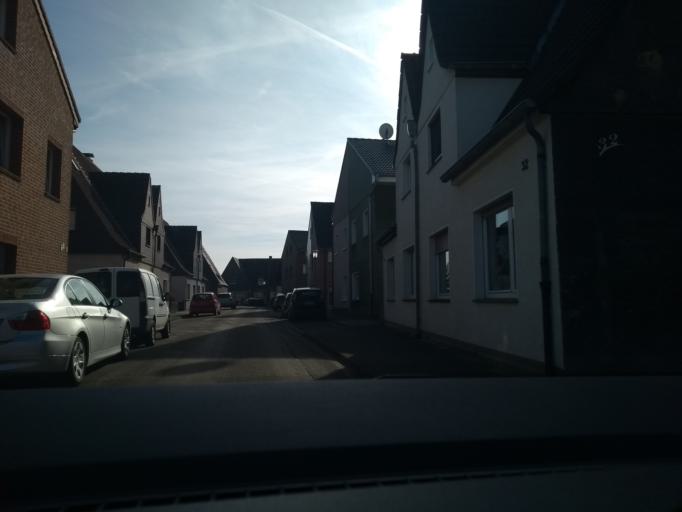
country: DE
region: North Rhine-Westphalia
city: Selm
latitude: 51.6921
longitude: 7.4618
